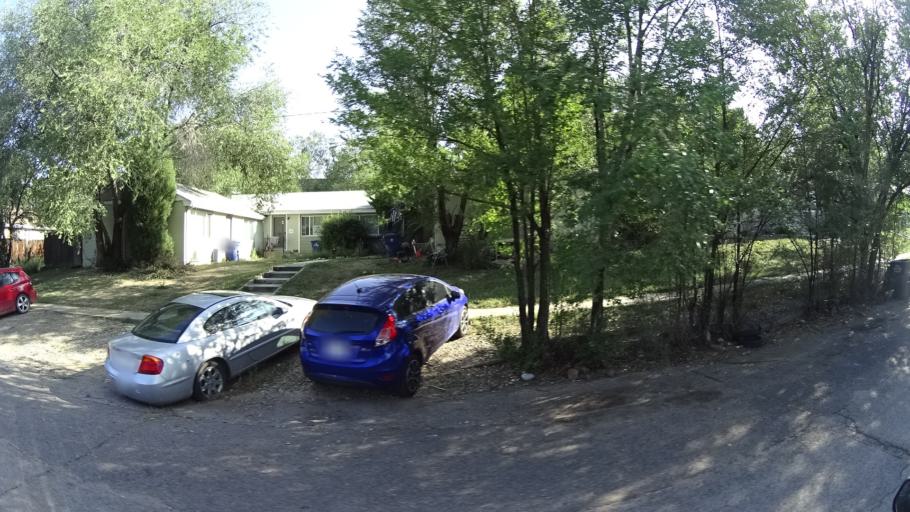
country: US
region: Colorado
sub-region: El Paso County
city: Colorado Springs
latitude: 38.8548
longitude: -104.8644
